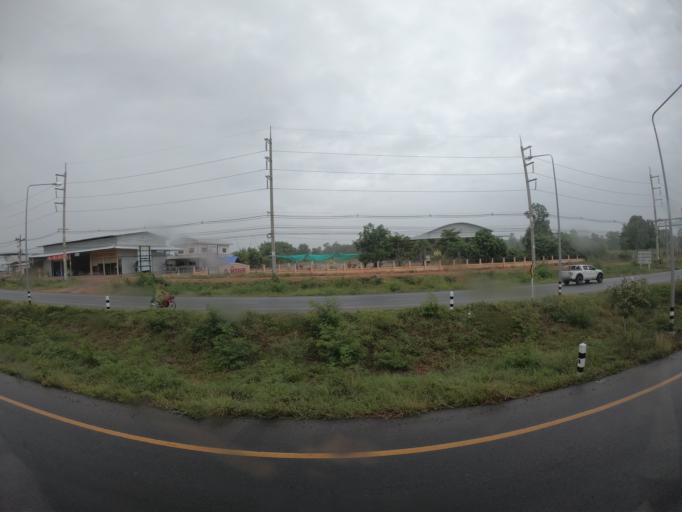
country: TH
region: Maha Sarakham
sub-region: Amphoe Borabue
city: Borabue
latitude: 16.0485
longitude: 103.0987
